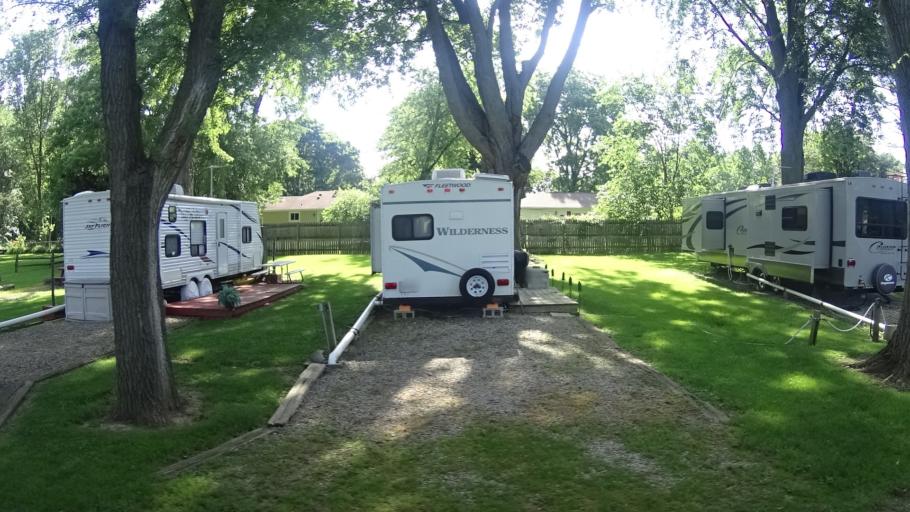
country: US
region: Ohio
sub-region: Erie County
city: Huron
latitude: 41.3803
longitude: -82.5002
